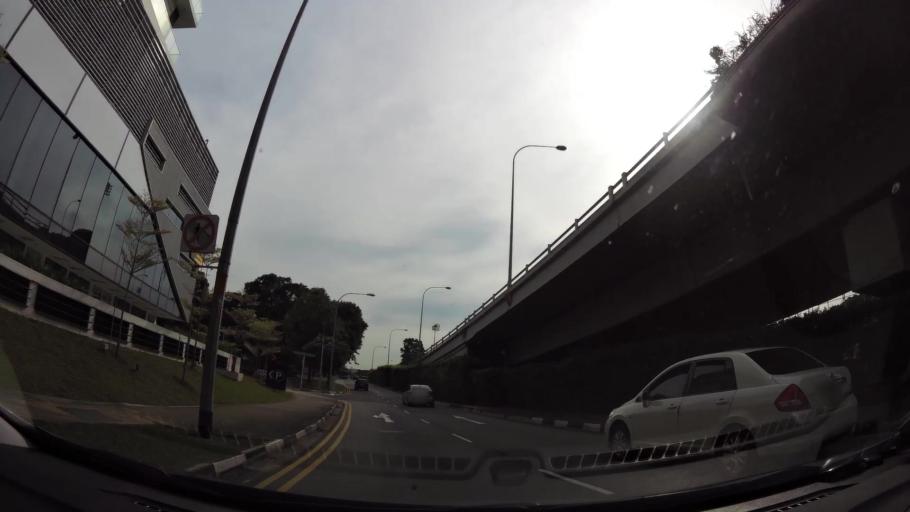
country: SG
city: Singapore
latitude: 1.3370
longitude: 103.7788
